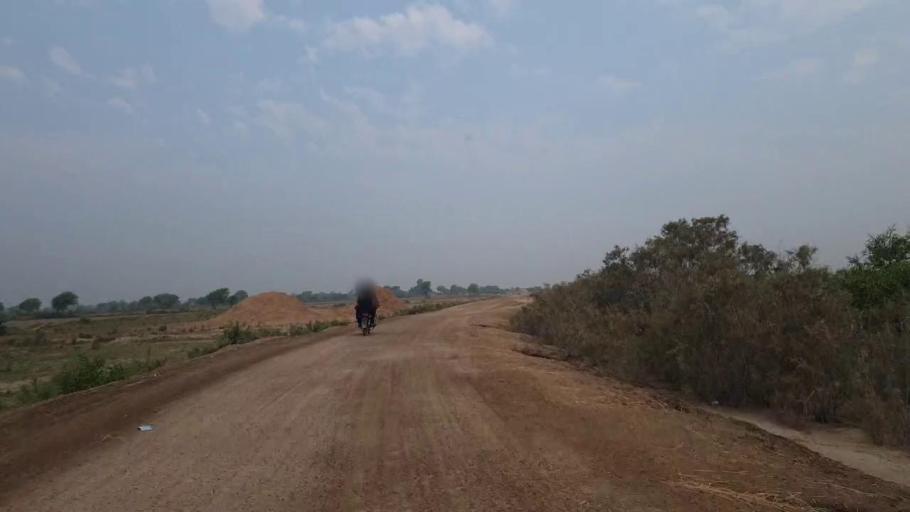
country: PK
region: Sindh
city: Tando Bago
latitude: 24.8014
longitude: 68.8738
